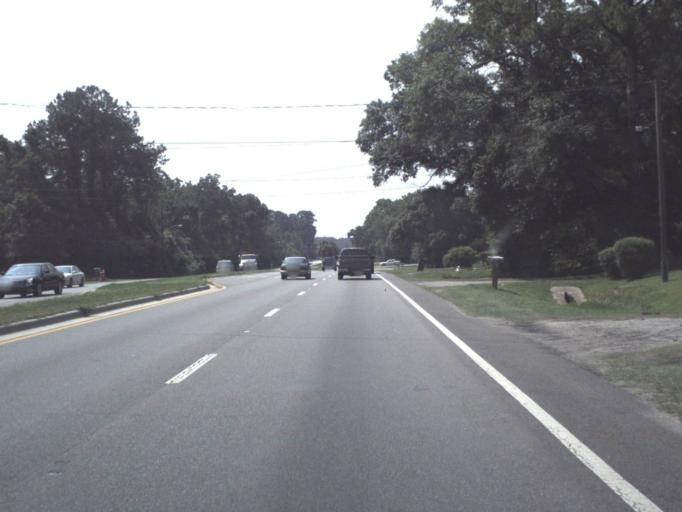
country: US
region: Florida
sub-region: Duval County
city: Jacksonville
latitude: 30.3786
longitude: -81.7288
